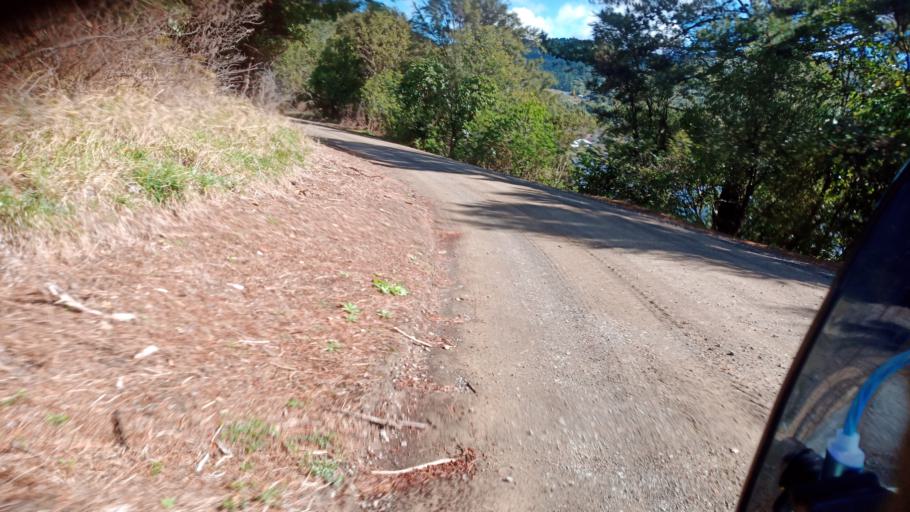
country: NZ
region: Hawke's Bay
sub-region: Wairoa District
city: Wairoa
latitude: -38.8134
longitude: 177.1539
